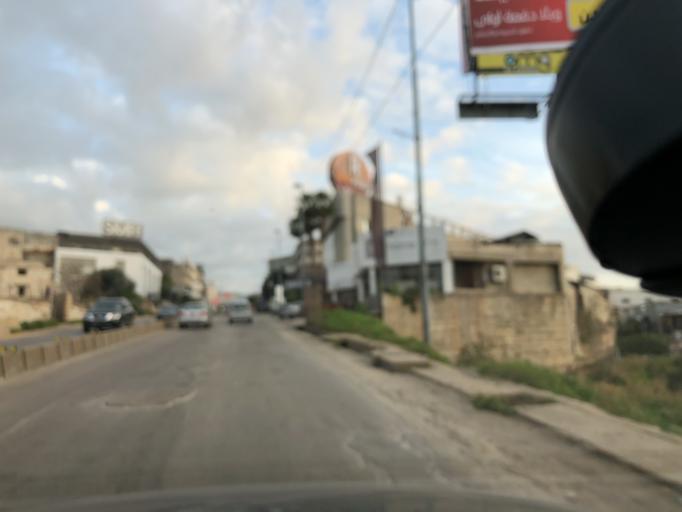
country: LB
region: Mont-Liban
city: Jdaidet el Matn
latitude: 33.8671
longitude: 35.5447
